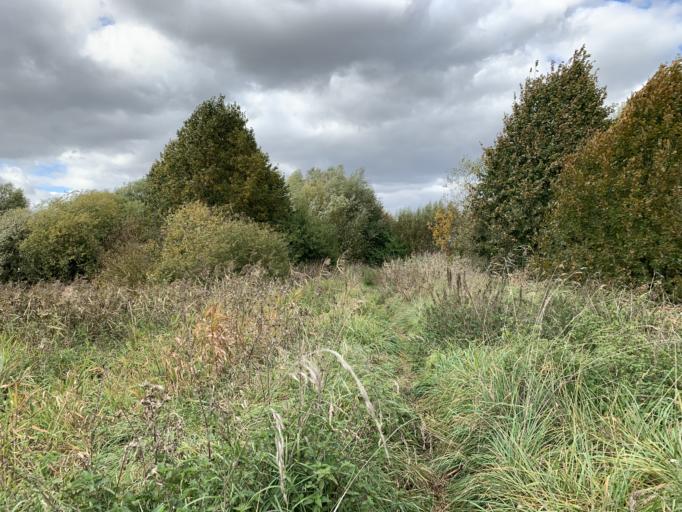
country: BY
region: Minsk
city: Nyasvizh
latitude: 53.2348
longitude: 26.7094
